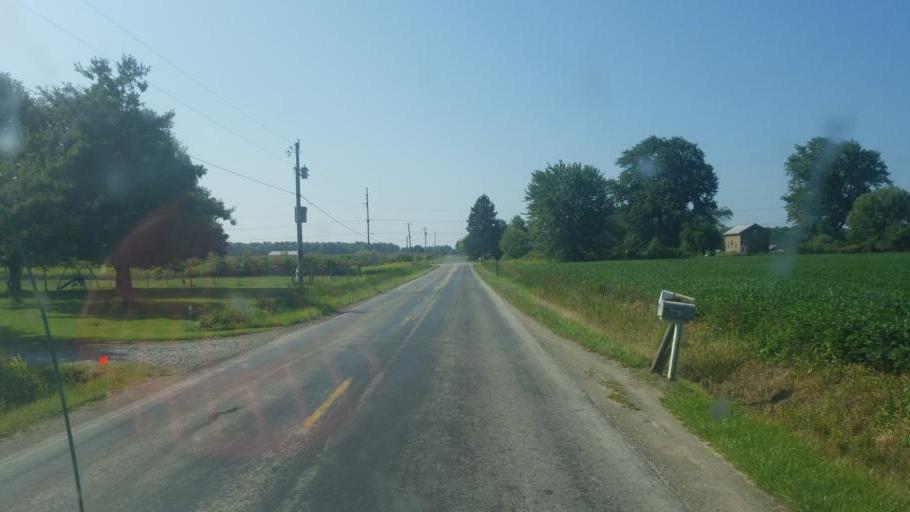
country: US
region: Ohio
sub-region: Wayne County
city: West Salem
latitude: 41.0296
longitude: -82.1823
